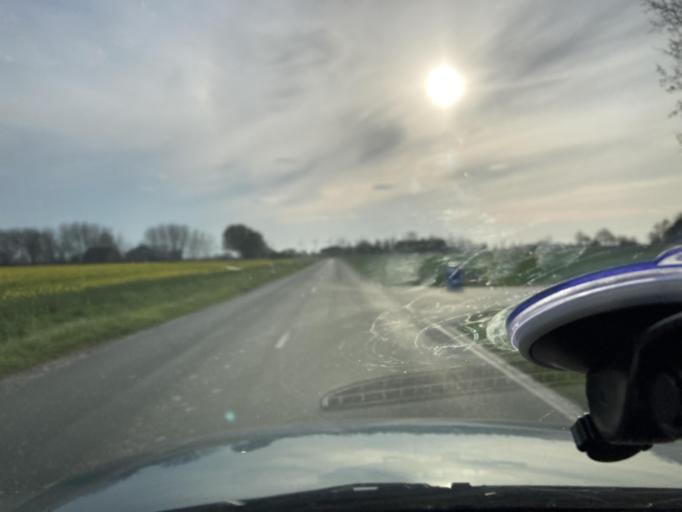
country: DE
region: Schleswig-Holstein
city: Schulp
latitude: 54.2540
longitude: 8.9483
